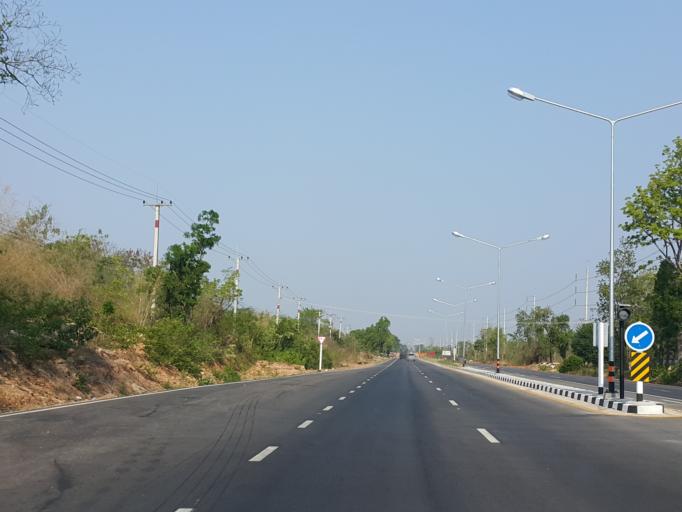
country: TH
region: Kanchanaburi
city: Kanchanaburi
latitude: 14.0872
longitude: 99.3630
